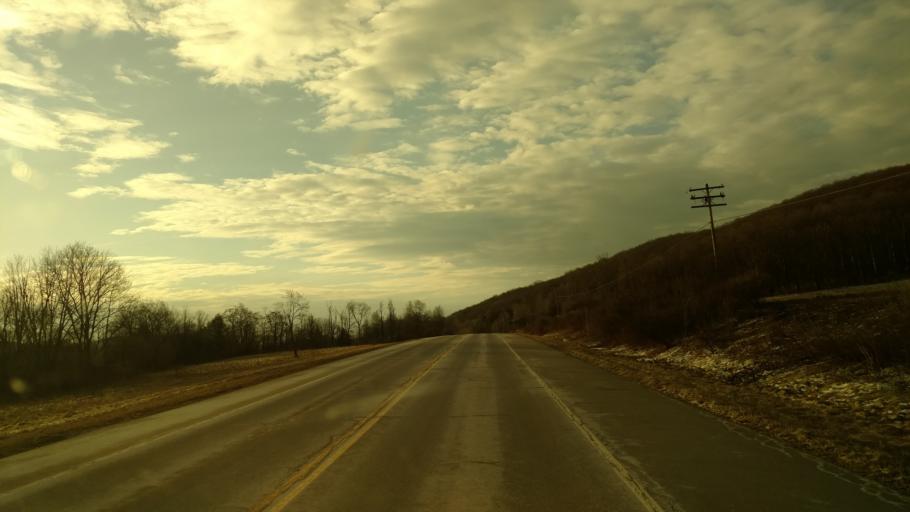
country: US
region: New York
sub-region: Allegany County
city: Wellsville
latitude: 42.0057
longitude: -77.8871
